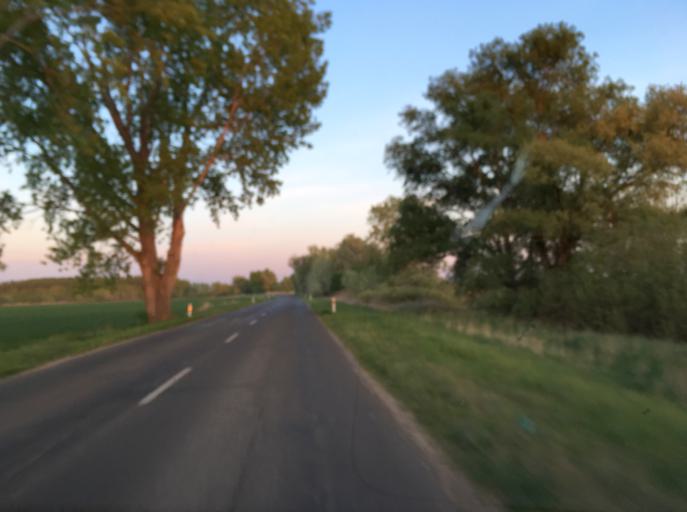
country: SK
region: Nitriansky
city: Kolarovo
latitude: 47.9187
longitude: 18.0432
